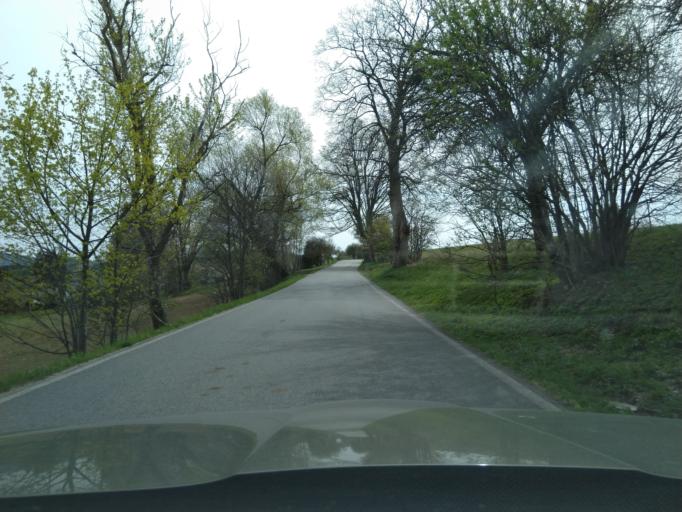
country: CZ
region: Jihocesky
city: Vacov
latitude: 49.1456
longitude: 13.7090
